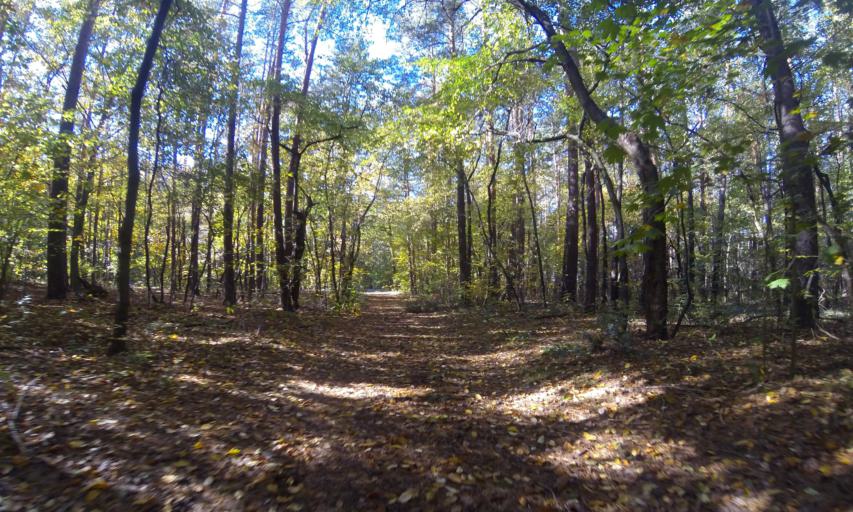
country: DE
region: Saxony
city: Weinbohla
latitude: 51.1992
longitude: 13.5928
